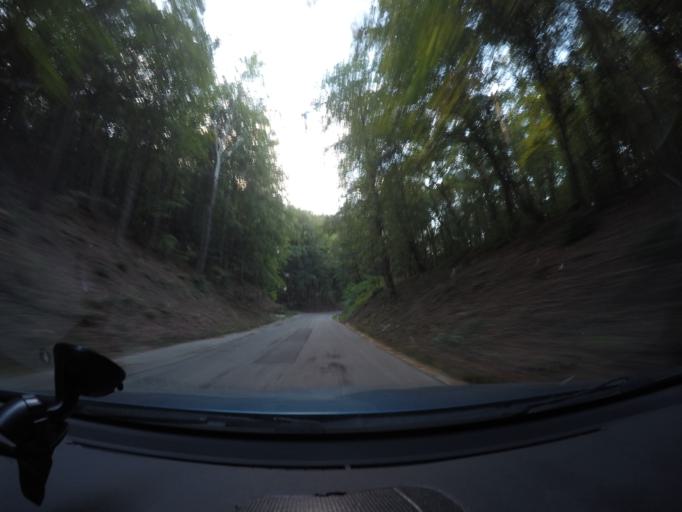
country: SK
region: Trenciansky
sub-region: Okres Trencin
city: Trencin
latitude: 48.8860
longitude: 18.0484
